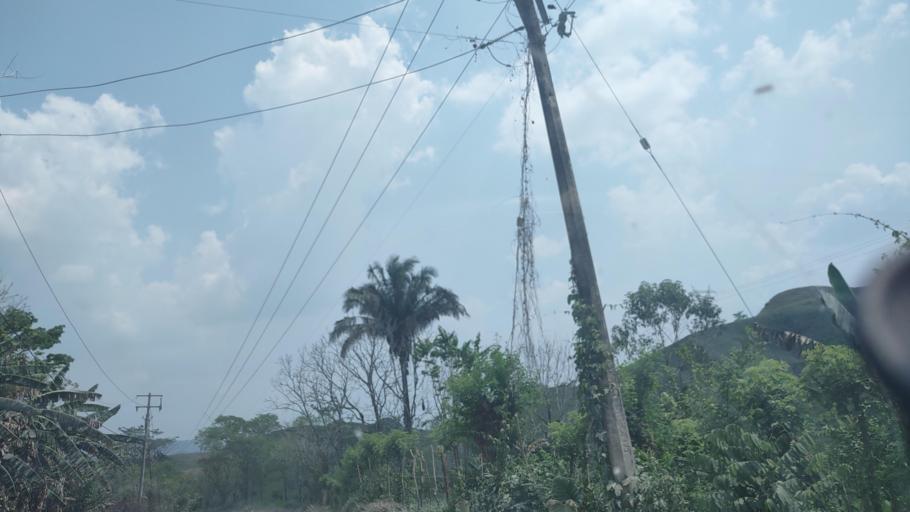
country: MX
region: Tabasco
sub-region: Huimanguillo
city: Francisco Rueda
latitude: 17.6026
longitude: -93.9047
